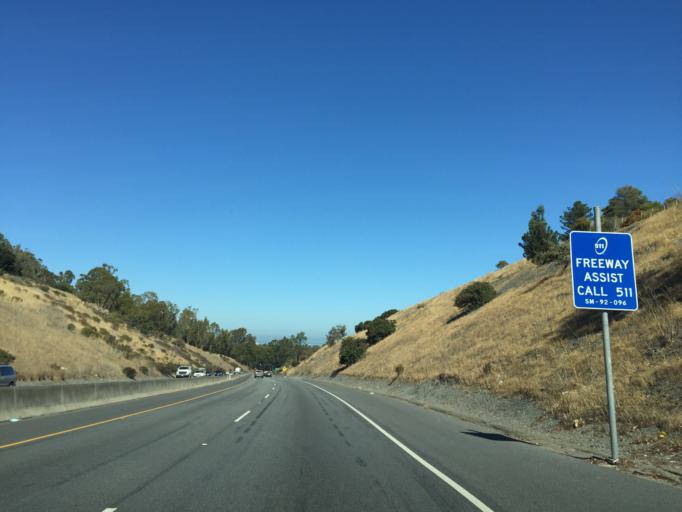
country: US
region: California
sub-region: San Mateo County
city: Highlands-Baywood Park
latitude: 37.5364
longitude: -122.3290
